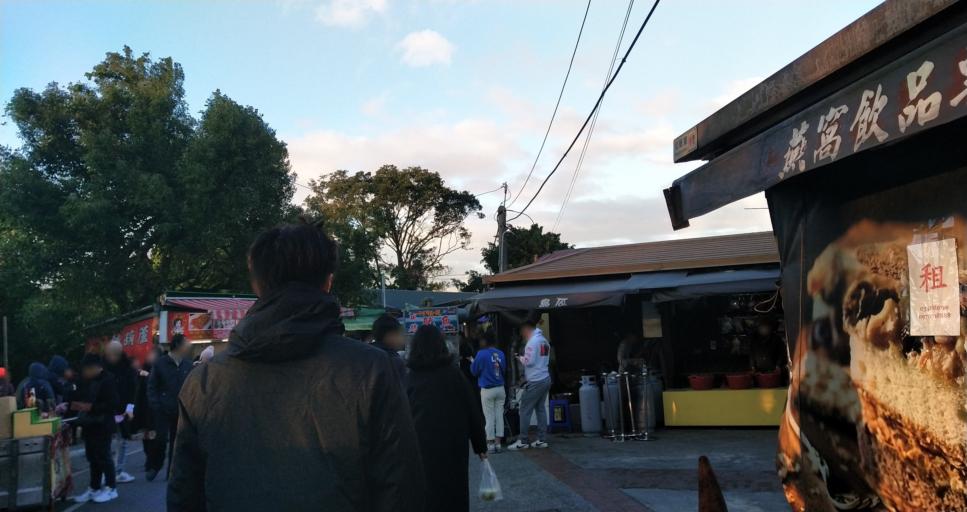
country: TW
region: Taiwan
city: Daxi
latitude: 24.8855
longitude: 121.2853
